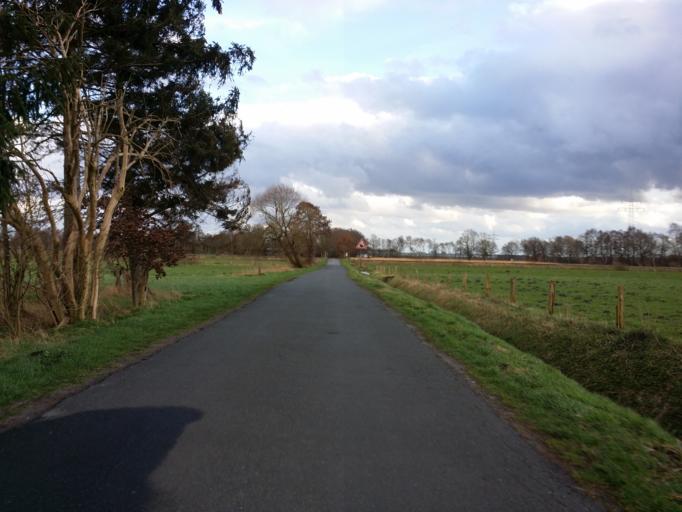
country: DE
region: Lower Saxony
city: Delmenhorst
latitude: 53.0192
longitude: 8.6297
